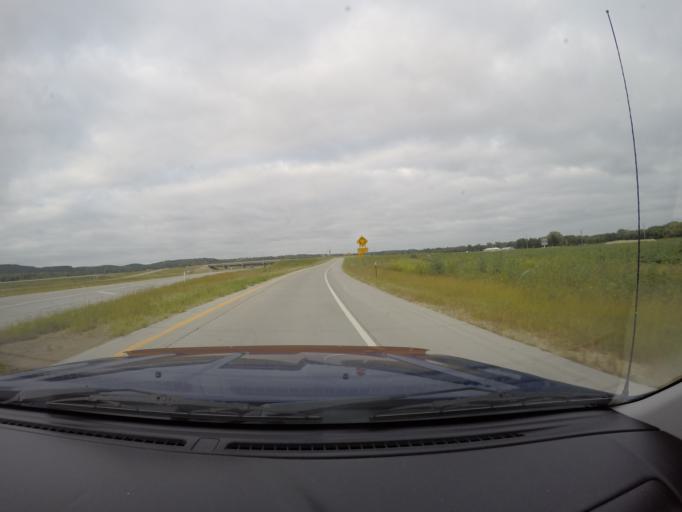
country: US
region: Kansas
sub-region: Riley County
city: Ogden
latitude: 39.1513
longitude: -96.6461
